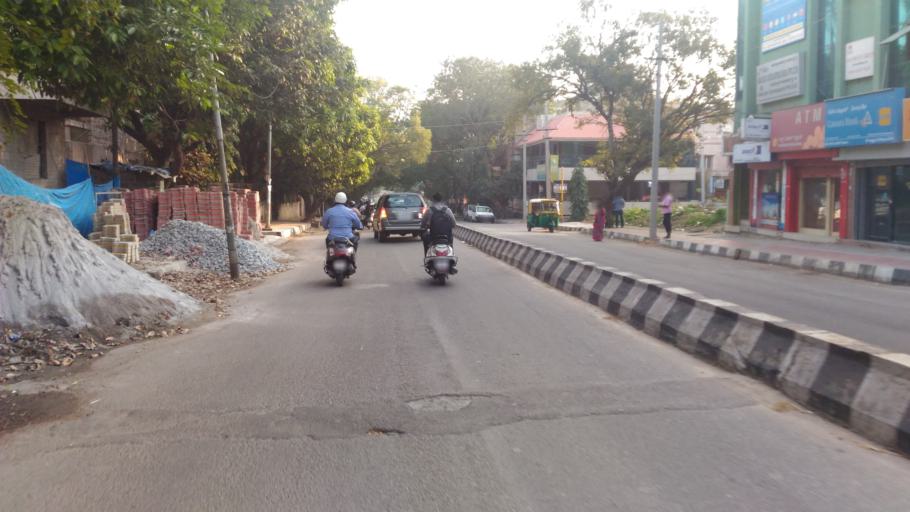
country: IN
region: Karnataka
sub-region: Bangalore Urban
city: Bangalore
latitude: 12.9079
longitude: 77.5952
